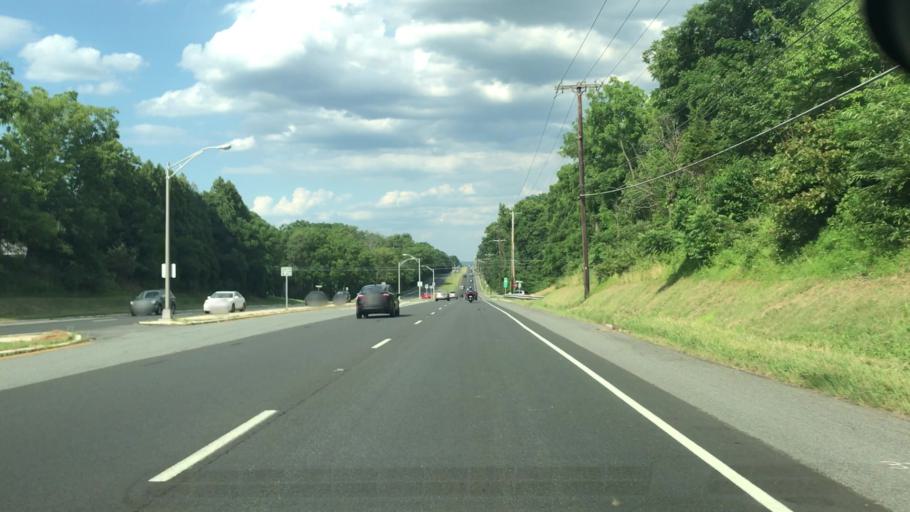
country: US
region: New Jersey
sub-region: Somerset County
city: Bradley Gardens
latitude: 40.5522
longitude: -74.7268
